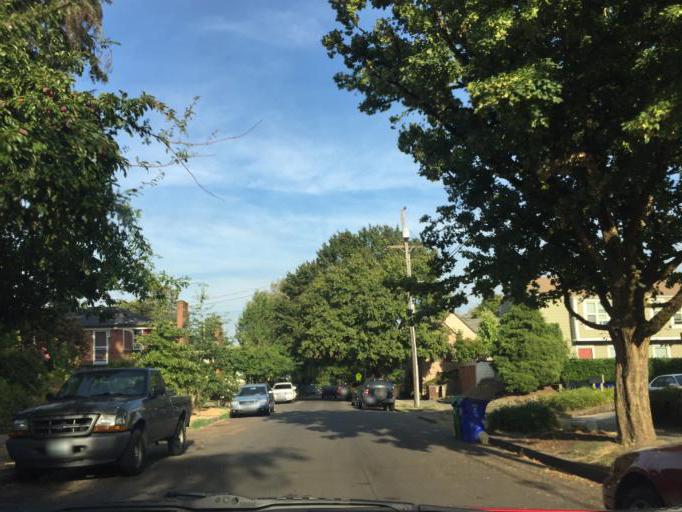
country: US
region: Oregon
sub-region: Multnomah County
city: Portland
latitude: 45.5250
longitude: -122.6425
